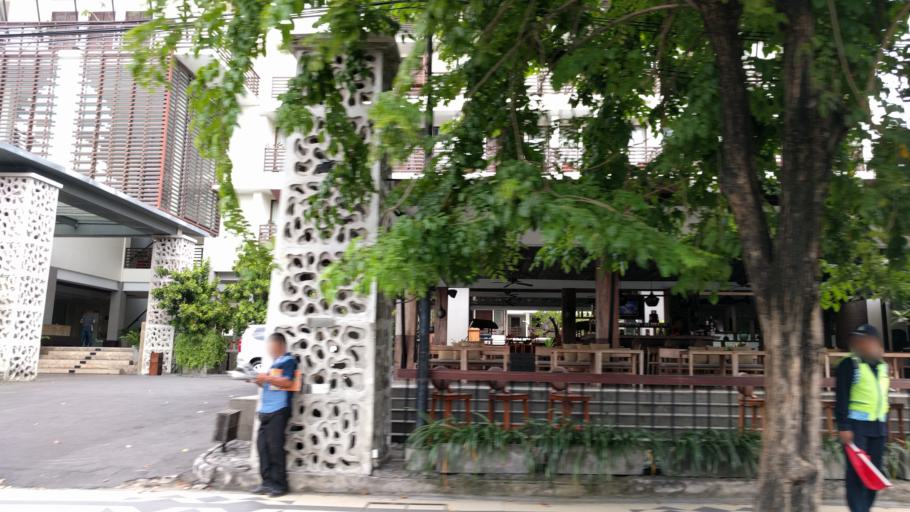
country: ID
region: Bali
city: Jabajero
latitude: -8.7307
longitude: 115.1678
